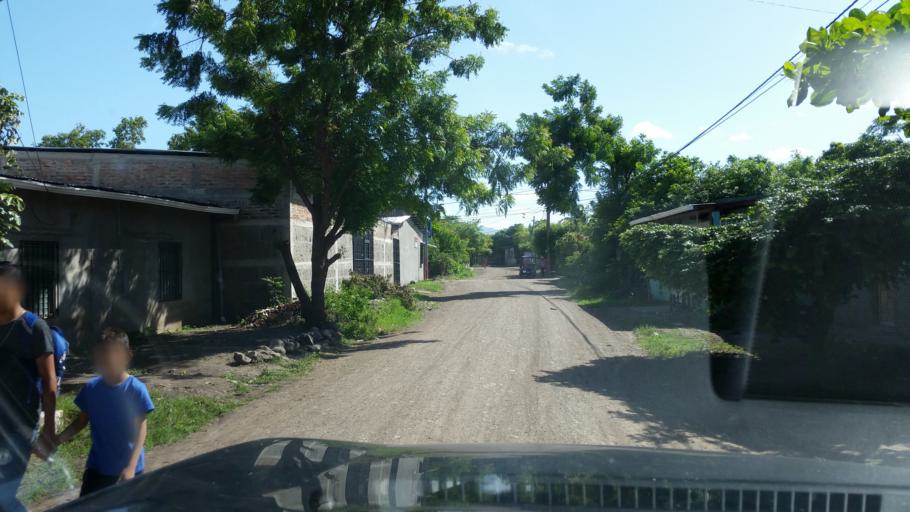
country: NI
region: Matagalpa
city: Ciudad Dario
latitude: 12.8608
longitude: -86.0930
